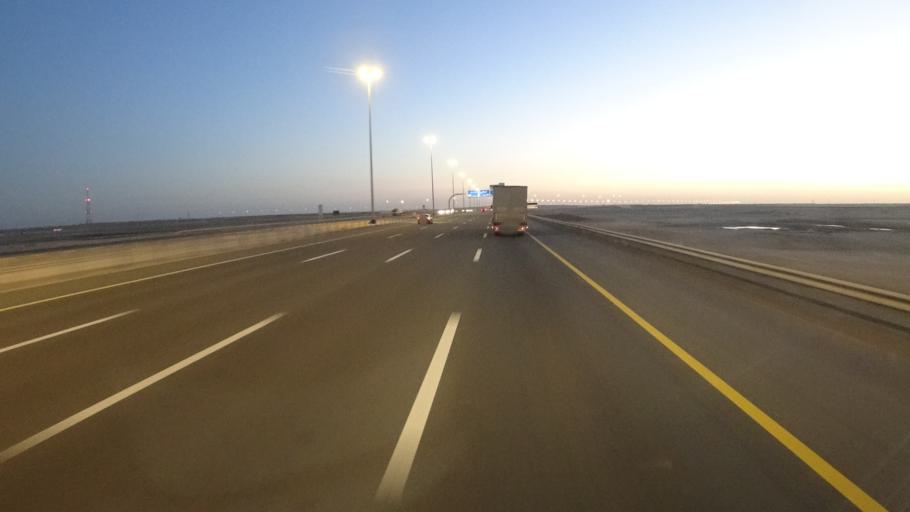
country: AE
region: Dubai
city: Dubai
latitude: 24.7756
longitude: 54.9536
